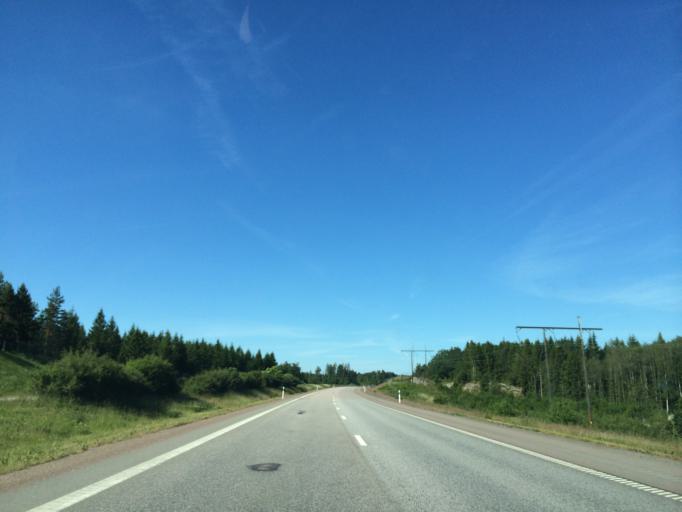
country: SE
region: OEstergoetland
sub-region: Vadstena Kommun
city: Herrestad
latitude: 58.2573
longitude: 14.8277
